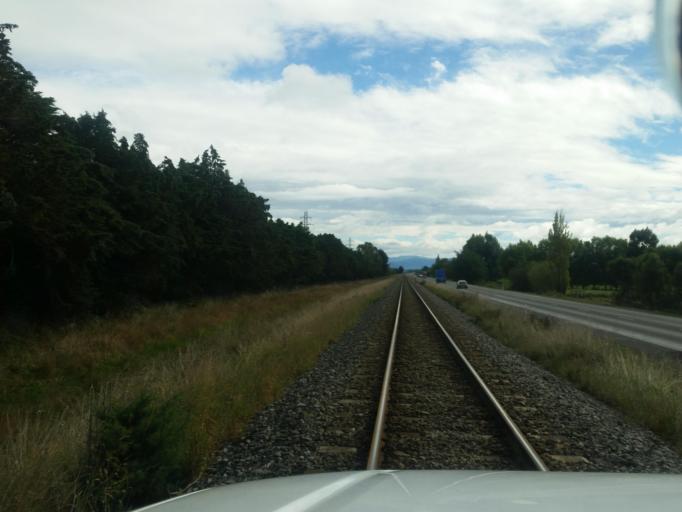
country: NZ
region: Canterbury
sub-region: Waimakariri District
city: Kaiapoi
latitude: -43.3632
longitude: 172.6341
